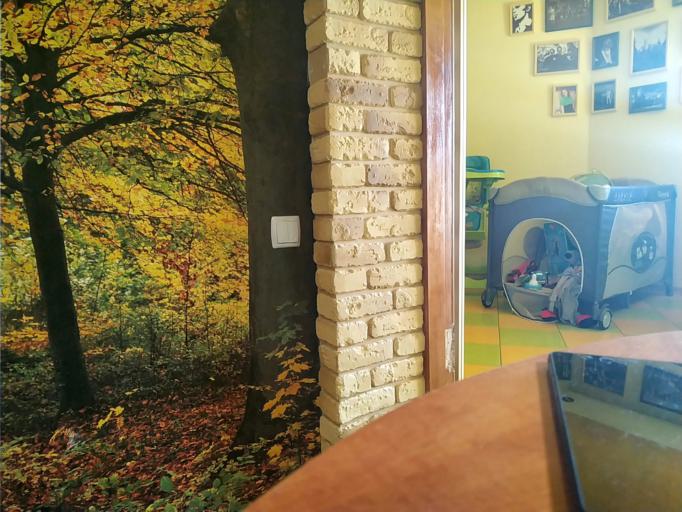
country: RU
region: Tverskaya
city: Krasnomayskiy
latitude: 57.6191
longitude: 34.4680
